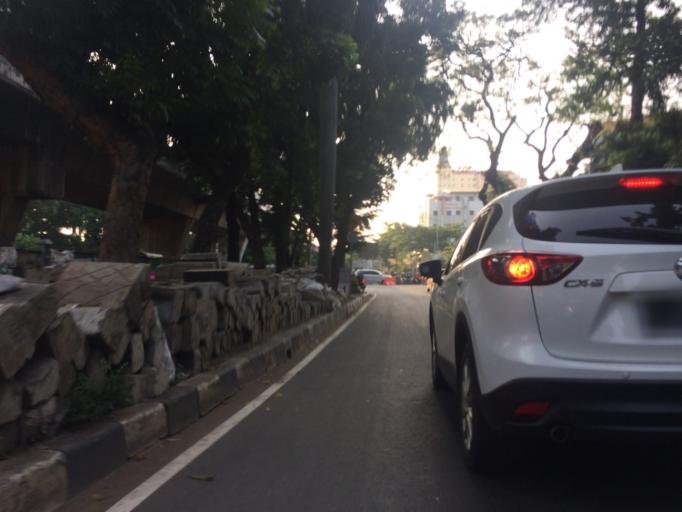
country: ID
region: Jakarta Raya
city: Jakarta
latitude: -6.2014
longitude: 106.8436
